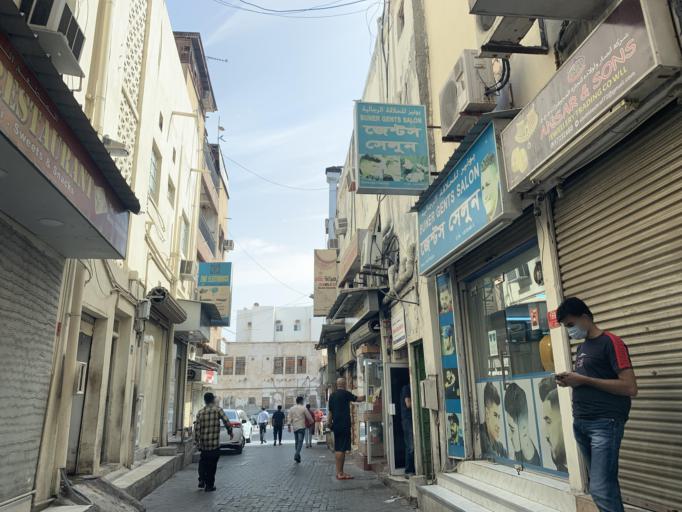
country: BH
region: Manama
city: Manama
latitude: 26.2326
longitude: 50.5784
